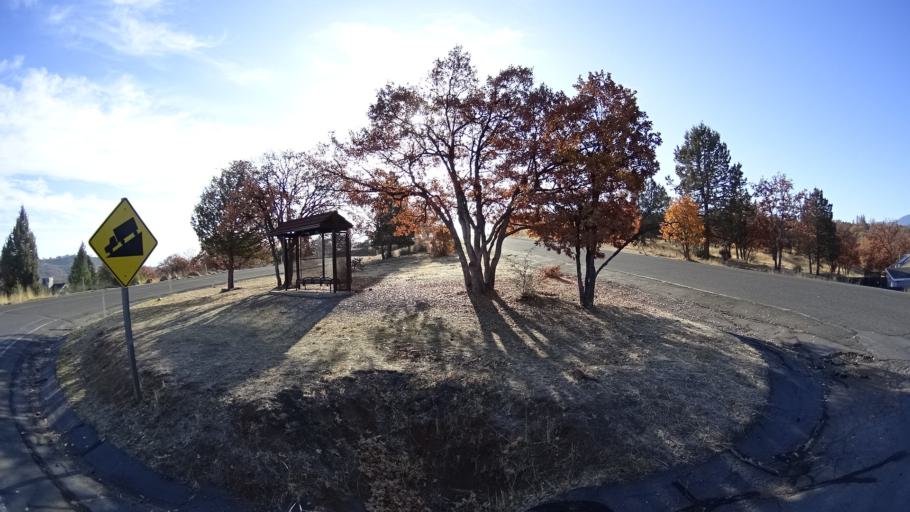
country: US
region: California
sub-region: Siskiyou County
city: Yreka
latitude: 41.7076
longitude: -122.6248
